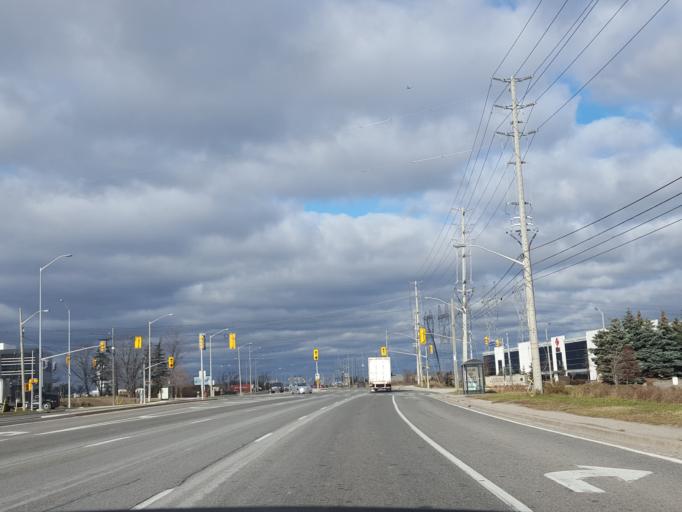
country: CA
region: Ontario
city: Brampton
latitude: 43.7199
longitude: -79.6640
